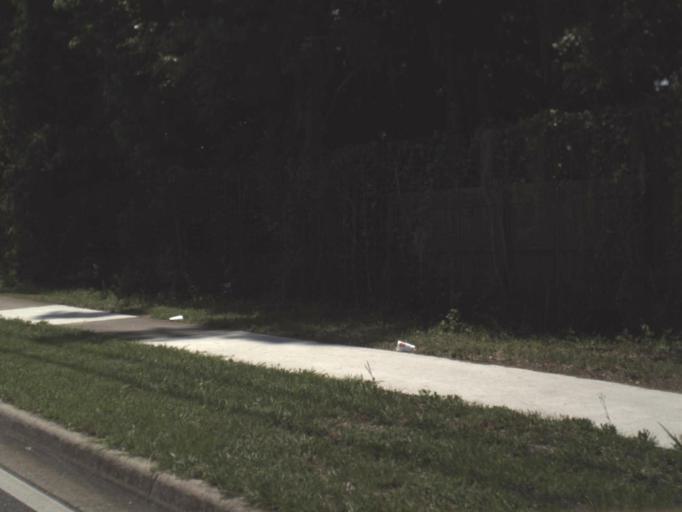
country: US
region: Florida
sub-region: Alachua County
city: Gainesville
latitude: 29.6365
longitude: -82.3329
